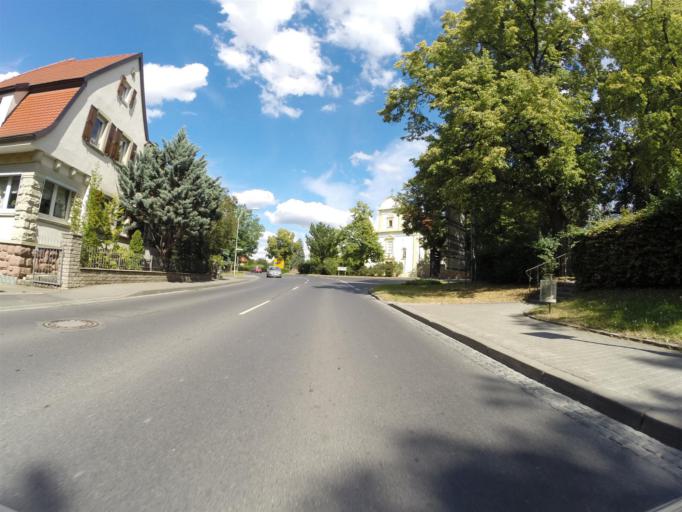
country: DE
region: Bavaria
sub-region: Regierungsbezirk Unterfranken
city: Gerolzhofen
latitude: 49.9038
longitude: 10.3493
